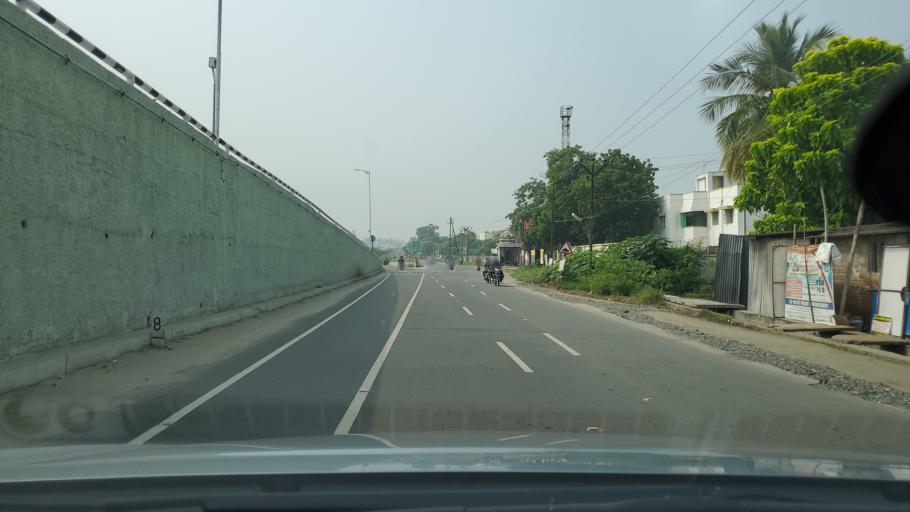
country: IN
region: Tamil Nadu
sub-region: Erode
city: Erode
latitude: 11.3180
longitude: 77.7130
